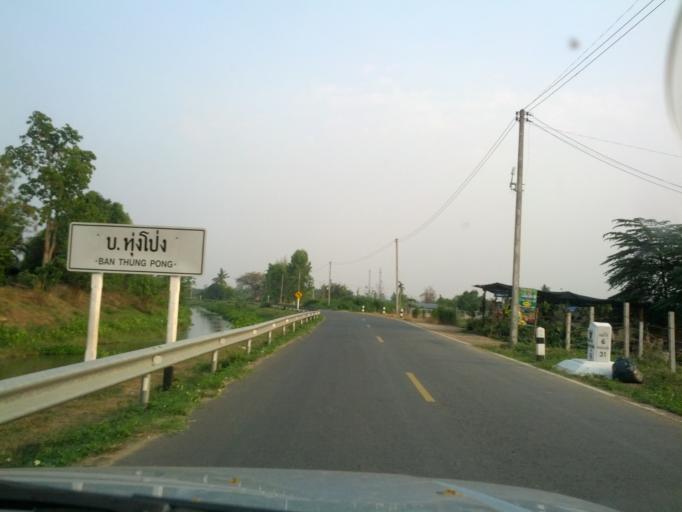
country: TH
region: Chiang Mai
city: San Sai
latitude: 18.9453
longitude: 98.9924
